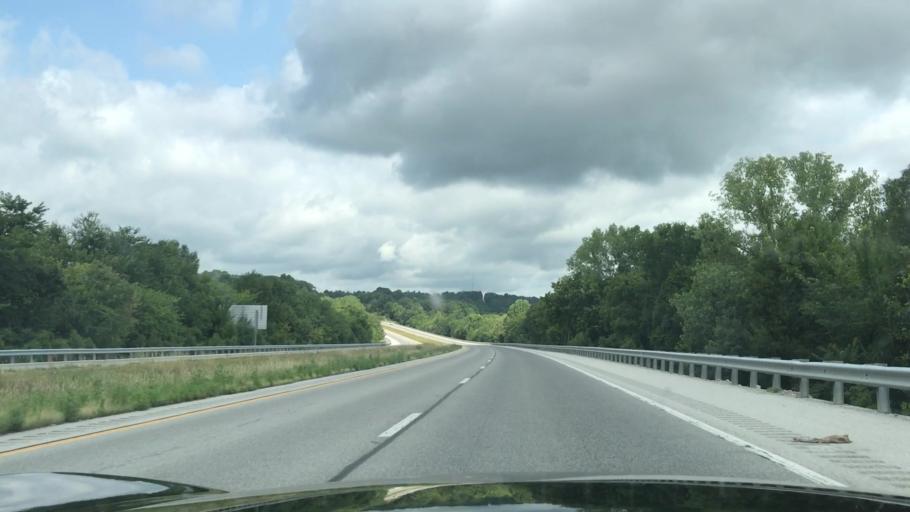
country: US
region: Kentucky
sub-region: Warren County
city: Bowling Green
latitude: 37.0077
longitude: -86.5094
